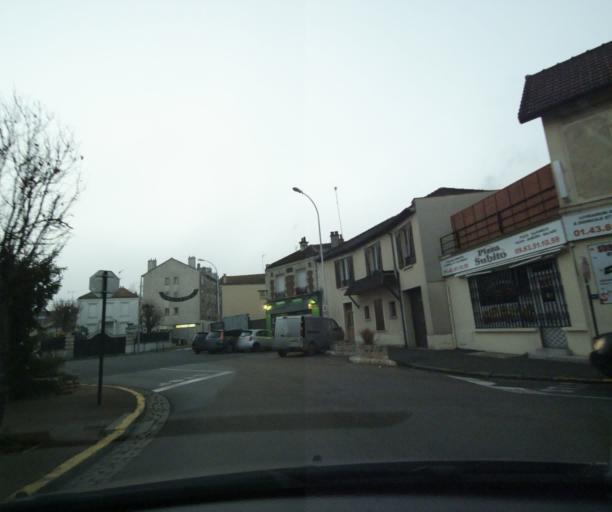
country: FR
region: Ile-de-France
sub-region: Departement de Seine-Saint-Denis
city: Neuilly-Plaisance
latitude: 48.8570
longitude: 2.5080
